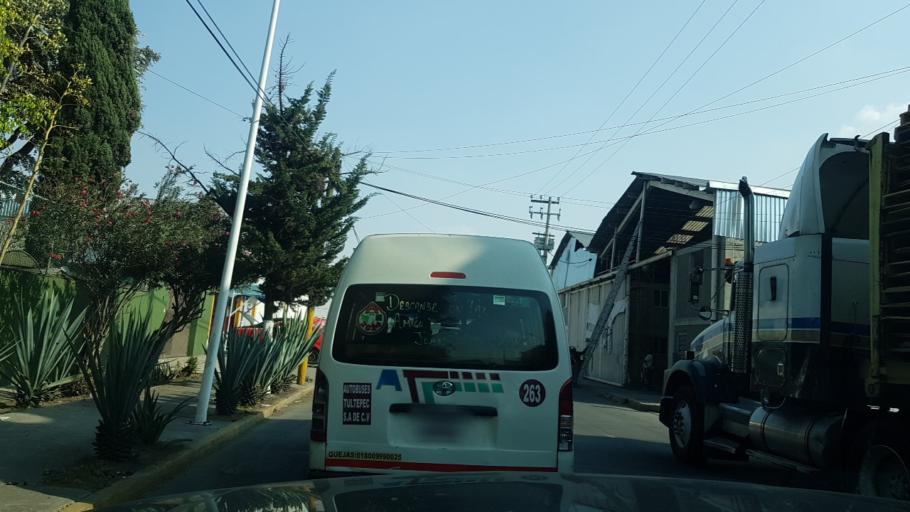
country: MX
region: Mexico
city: Santiago Teyahualco
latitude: 19.6576
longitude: -99.1249
